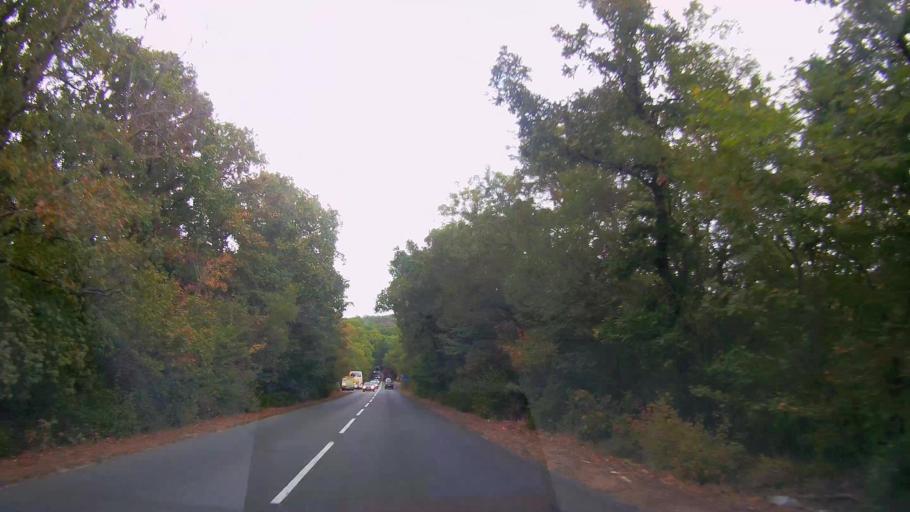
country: BG
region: Burgas
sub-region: Obshtina Primorsko
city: Primorsko
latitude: 42.2991
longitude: 27.7295
